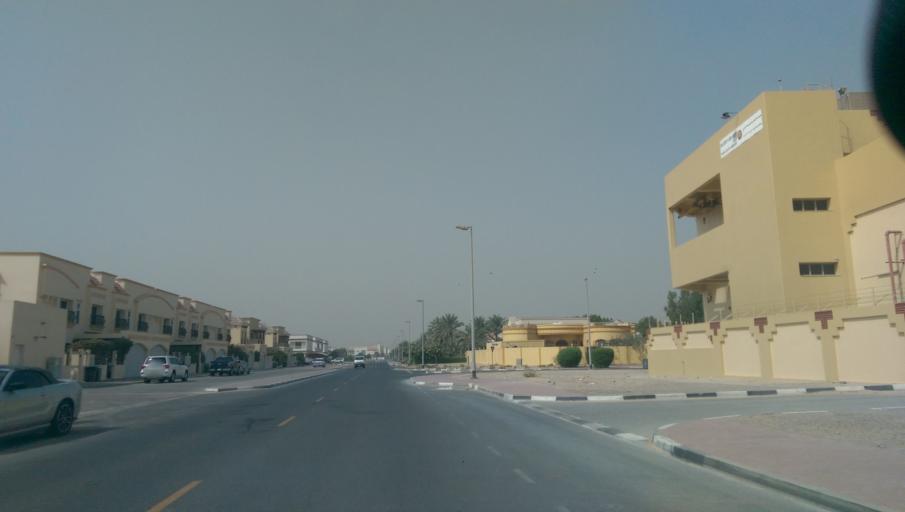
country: AE
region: Dubai
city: Dubai
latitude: 25.1542
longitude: 55.2236
